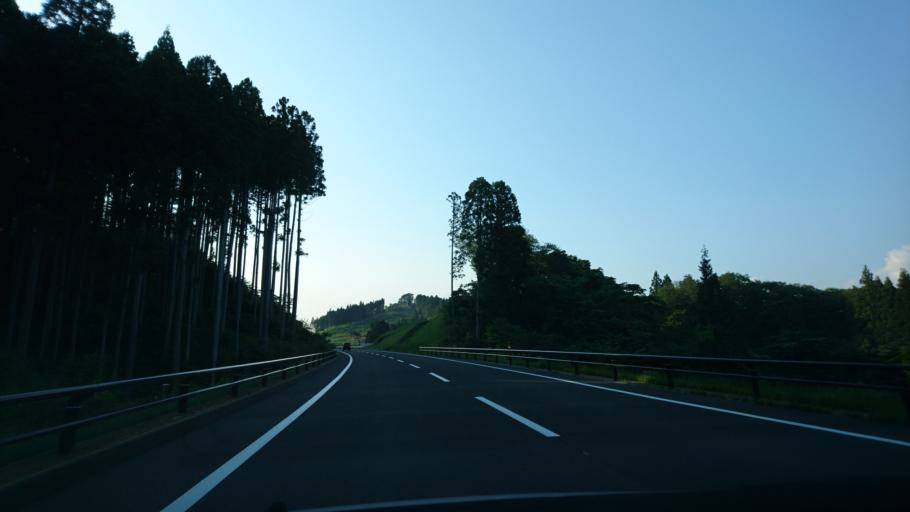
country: JP
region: Iwate
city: Ofunato
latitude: 38.9233
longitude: 141.4559
